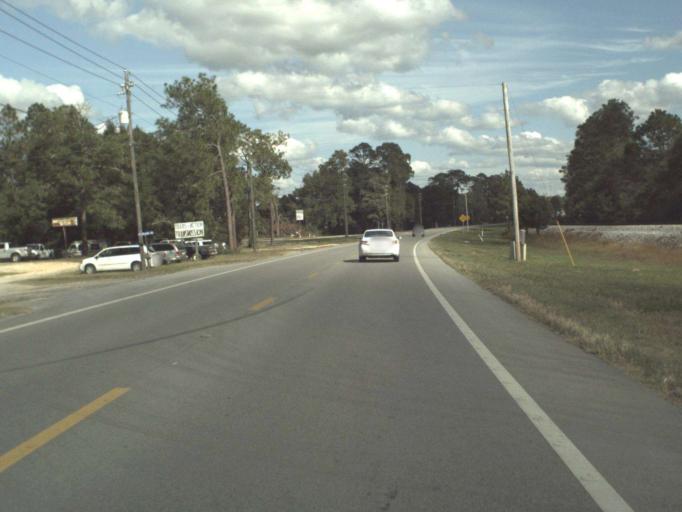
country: US
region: Florida
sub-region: Walton County
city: DeFuniak Springs
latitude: 30.7278
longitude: -86.0826
